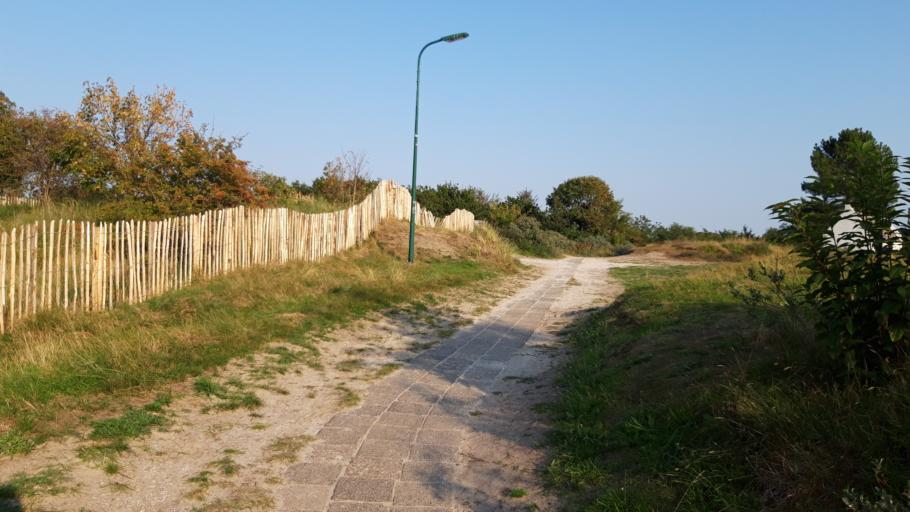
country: NL
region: Friesland
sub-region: Gemeente Schiermonnikoog
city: Schiermonnikoog
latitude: 53.4813
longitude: 6.1582
